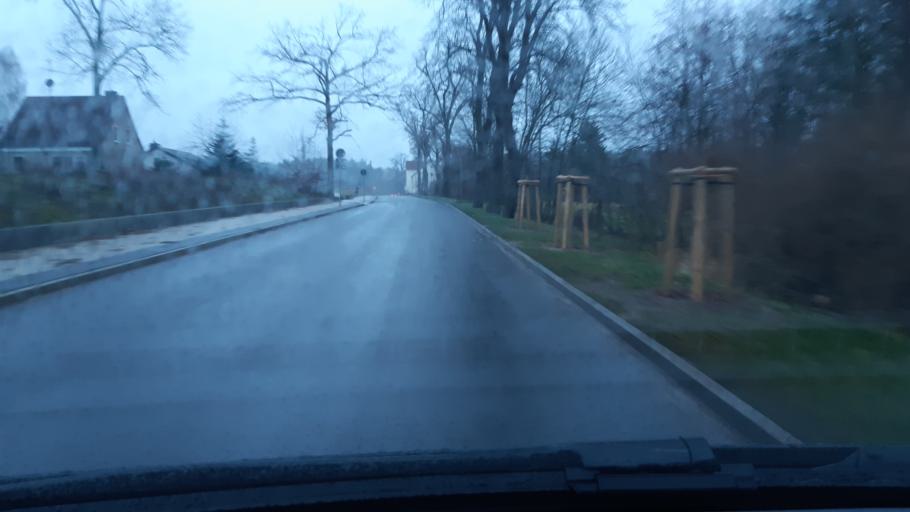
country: DE
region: Brandenburg
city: Milmersdorf
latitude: 53.1145
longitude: 13.6416
